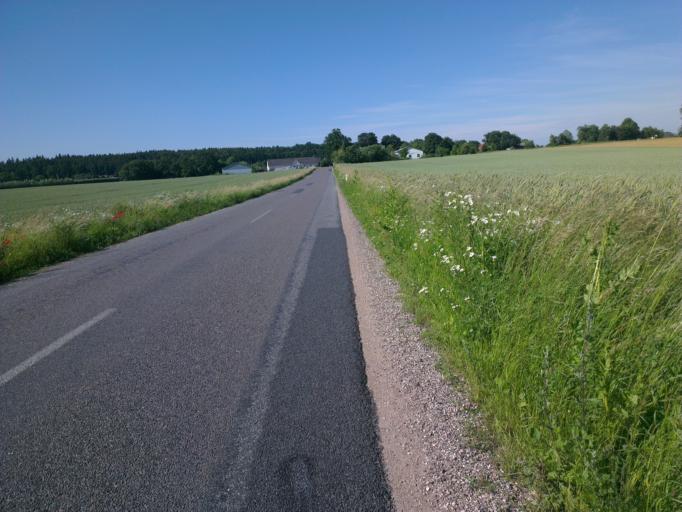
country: DK
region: Capital Region
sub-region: Frederikssund Kommune
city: Skibby
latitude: 55.7979
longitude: 11.9600
